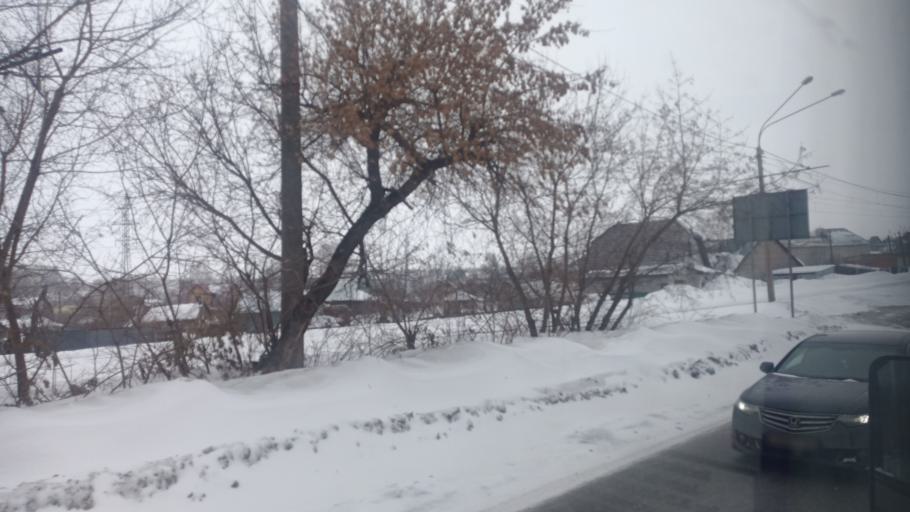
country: RU
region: Altai Krai
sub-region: Gorod Barnaulskiy
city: Barnaul
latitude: 53.3877
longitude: 83.6810
